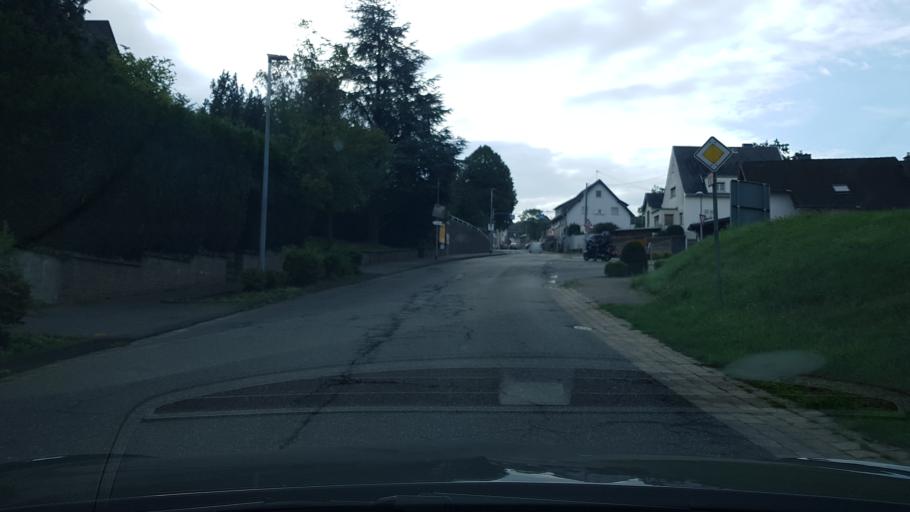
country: DE
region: Rheinland-Pfalz
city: Munstermaifeld
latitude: 50.2493
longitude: 7.3585
